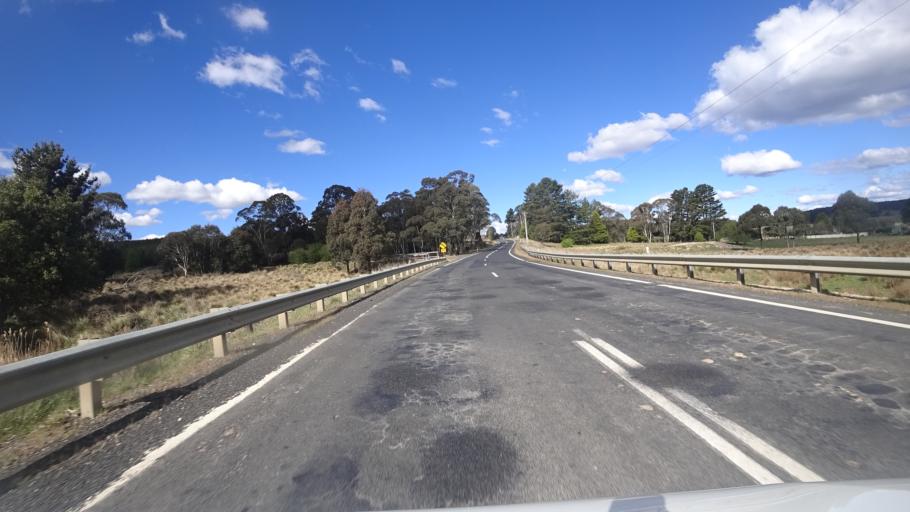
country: AU
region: New South Wales
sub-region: Oberon
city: Oberon
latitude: -33.6823
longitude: 150.0369
